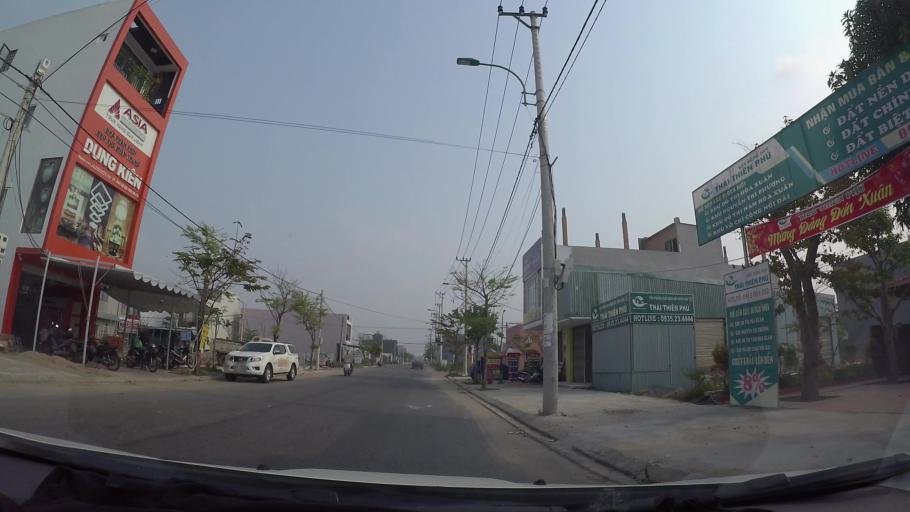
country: VN
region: Da Nang
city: Ngu Hanh Son
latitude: 16.0087
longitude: 108.2290
